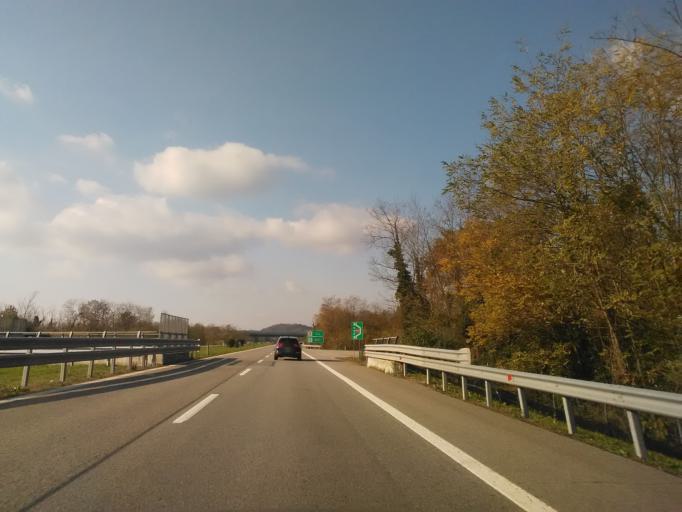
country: IT
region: Piedmont
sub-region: Provincia di Vercelli
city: Alice Castello
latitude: 45.3790
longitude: 8.0759
